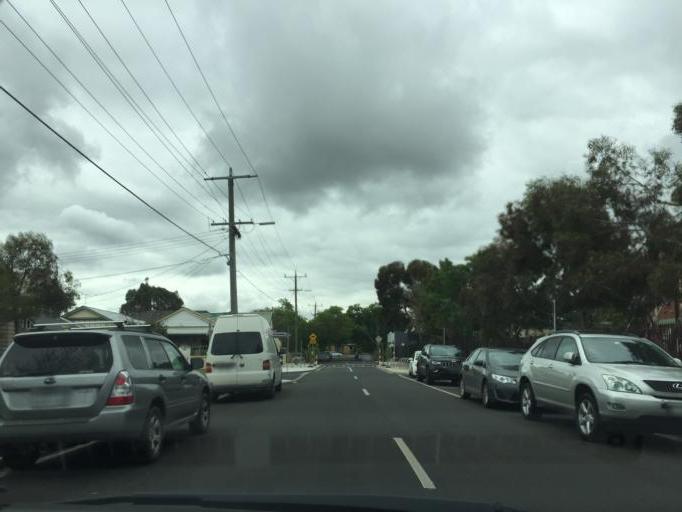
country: AU
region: Victoria
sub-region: Maribyrnong
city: West Footscray
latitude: -37.7949
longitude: 144.8751
